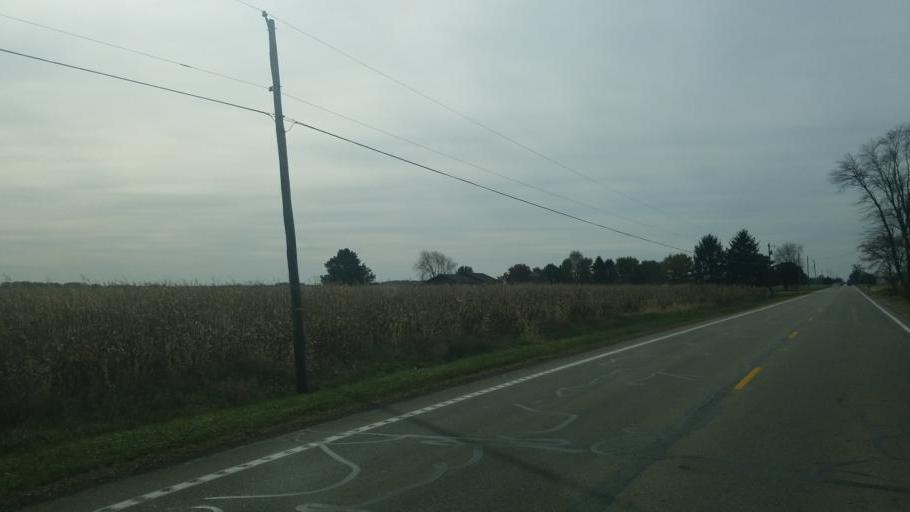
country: US
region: Ohio
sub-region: Madison County
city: West Jefferson
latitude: 40.0092
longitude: -83.3129
